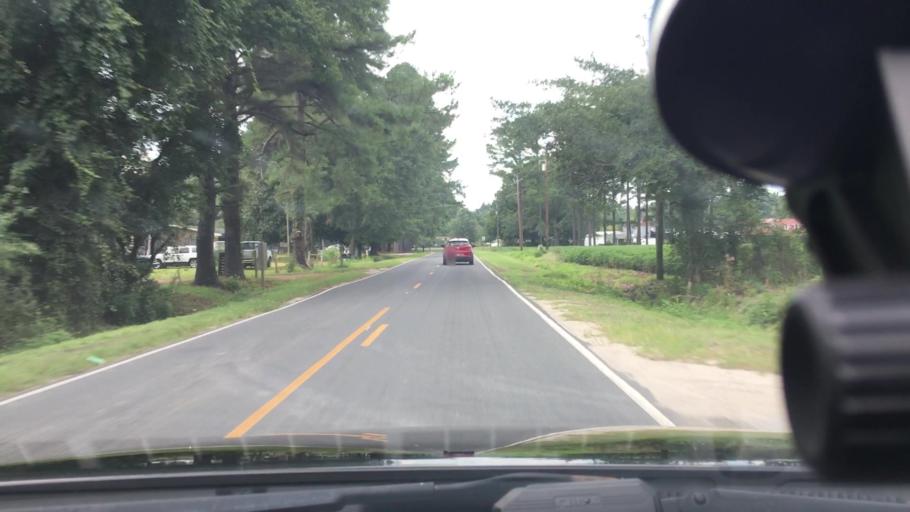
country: US
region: North Carolina
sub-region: Craven County
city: New Bern
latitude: 35.1712
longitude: -77.0509
